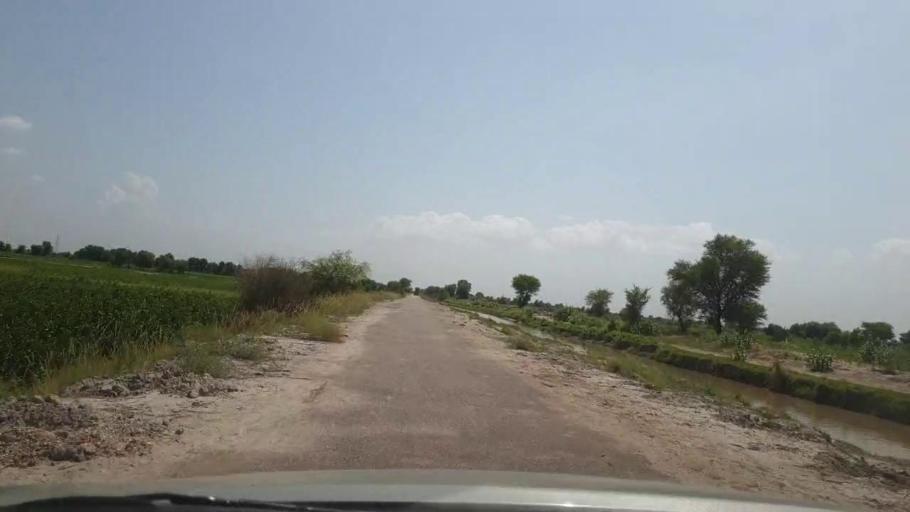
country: PK
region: Sindh
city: Pano Aqil
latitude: 27.7244
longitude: 69.0882
